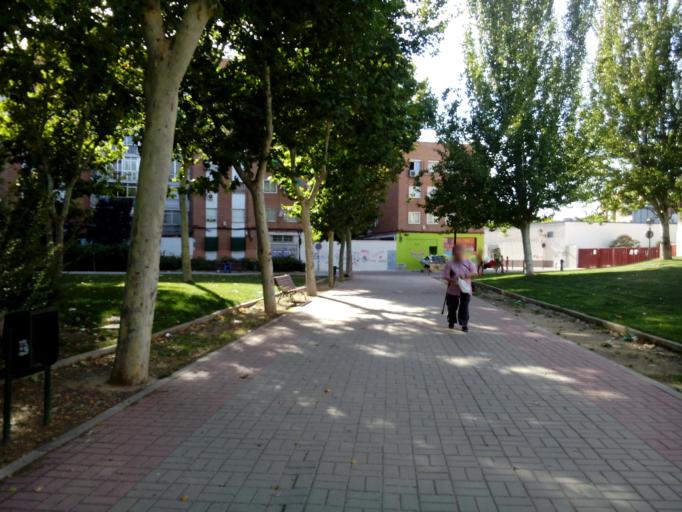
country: ES
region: Madrid
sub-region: Provincia de Madrid
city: Carabanchel
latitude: 40.3938
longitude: -3.7143
